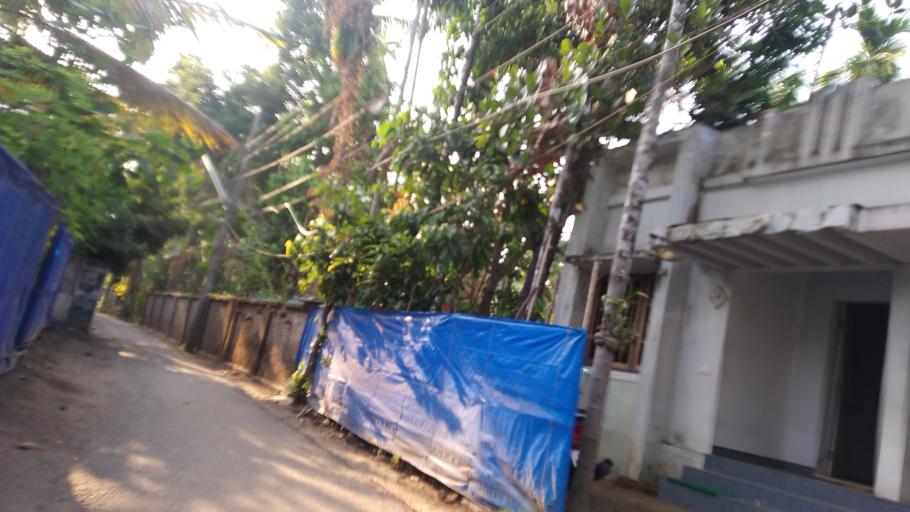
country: IN
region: Kerala
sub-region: Ernakulam
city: Elur
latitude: 10.0882
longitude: 76.2115
